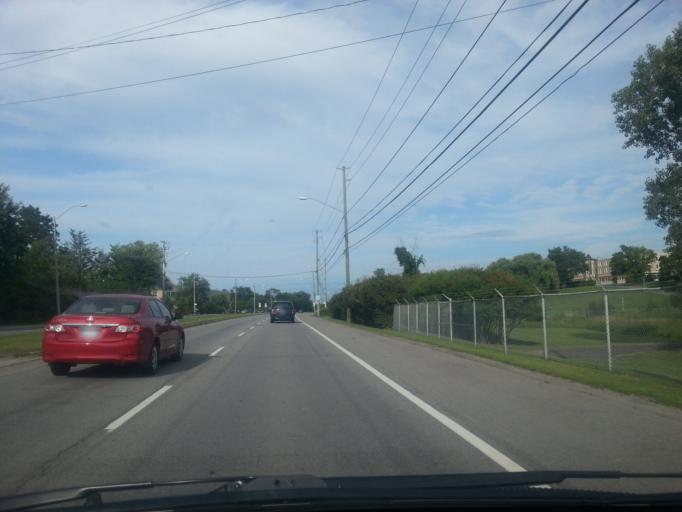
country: CA
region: Quebec
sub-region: Outaouais
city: Gatineau
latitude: 45.4590
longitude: -75.5626
